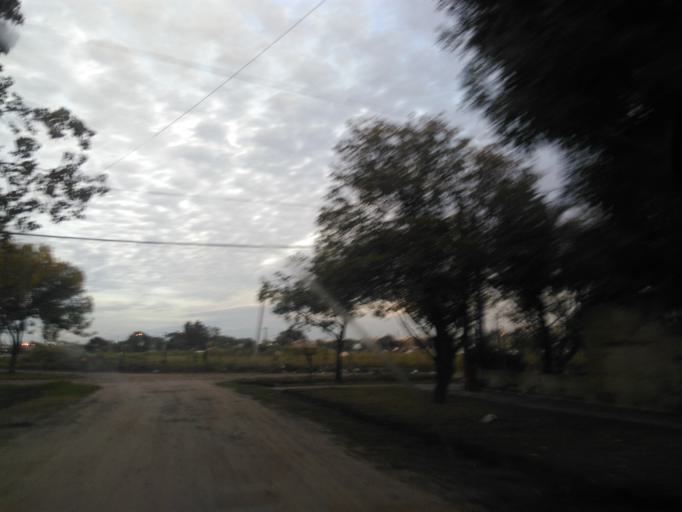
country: AR
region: Chaco
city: Resistencia
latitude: -27.4717
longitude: -58.9843
